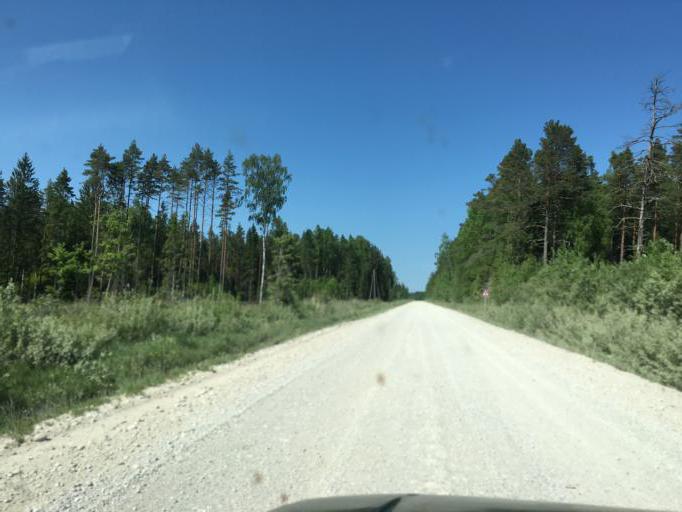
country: LV
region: Dundaga
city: Dundaga
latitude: 57.4390
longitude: 22.3183
